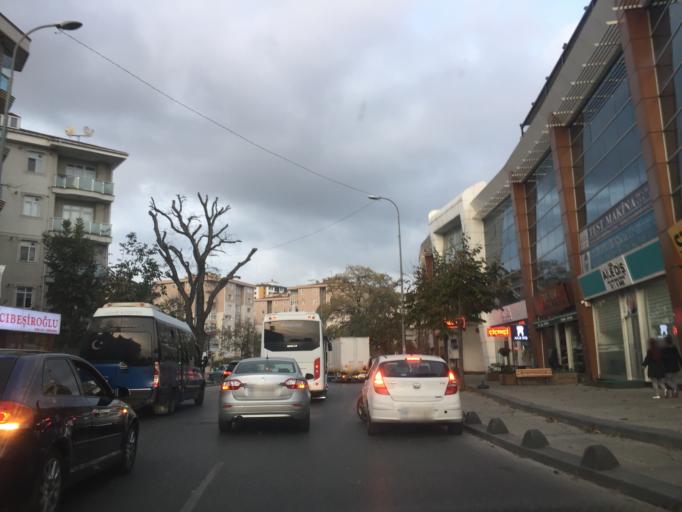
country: TR
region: Istanbul
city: Samandira
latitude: 40.9851
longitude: 29.2325
